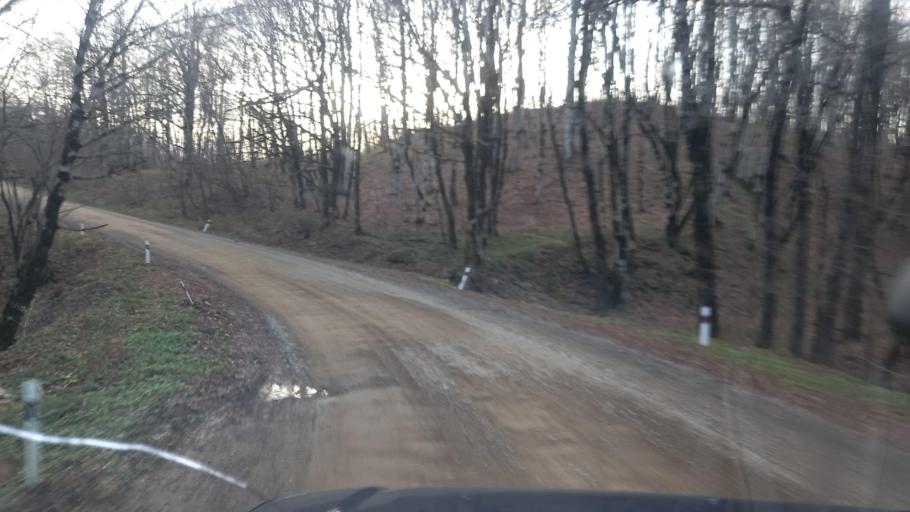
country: RU
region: Krasnodarskiy
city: Agoy
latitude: 44.3414
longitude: 39.2545
